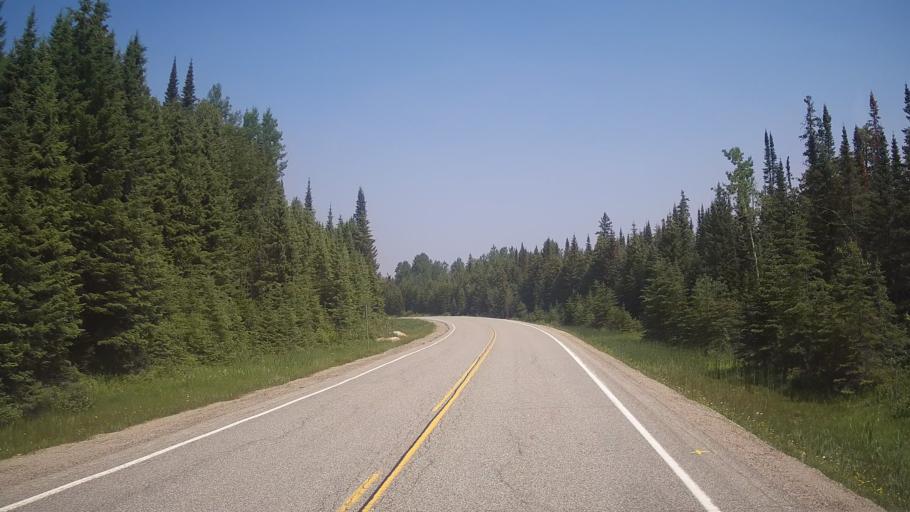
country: CA
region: Ontario
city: Timmins
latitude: 48.2158
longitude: -81.5720
